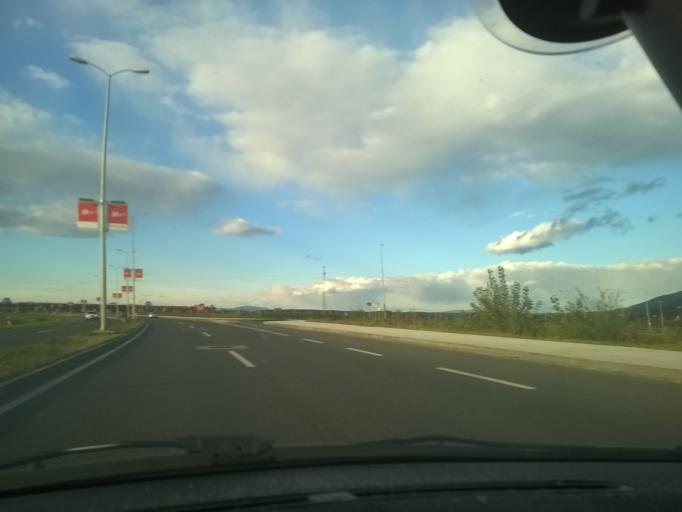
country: HR
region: Zagrebacka
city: Zapresic
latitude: 45.8622
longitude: 15.8279
